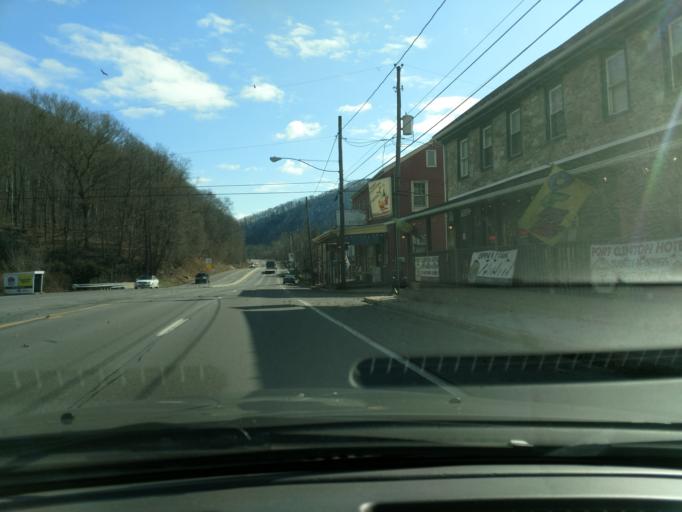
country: US
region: Pennsylvania
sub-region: Berks County
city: West Hamburg
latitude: 40.5826
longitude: -76.0245
